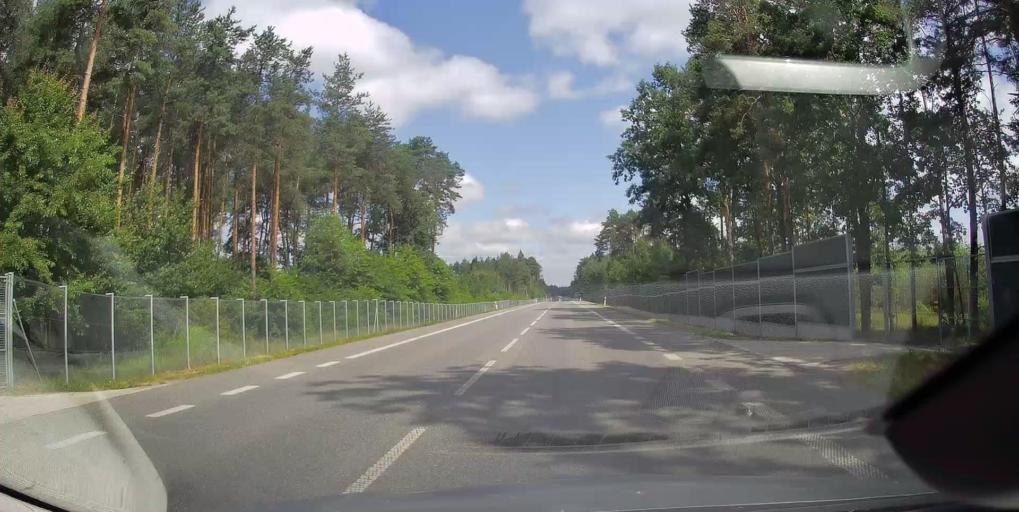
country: PL
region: Subcarpathian Voivodeship
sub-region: Powiat mielecki
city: Mielec
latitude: 50.3010
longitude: 21.4958
